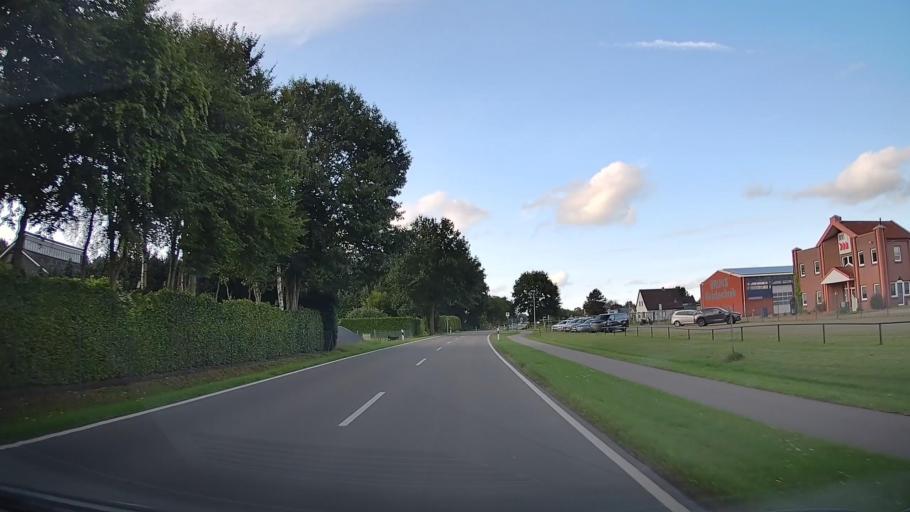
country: DE
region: Lower Saxony
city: Hilkenbrook
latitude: 53.0589
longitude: 7.7247
